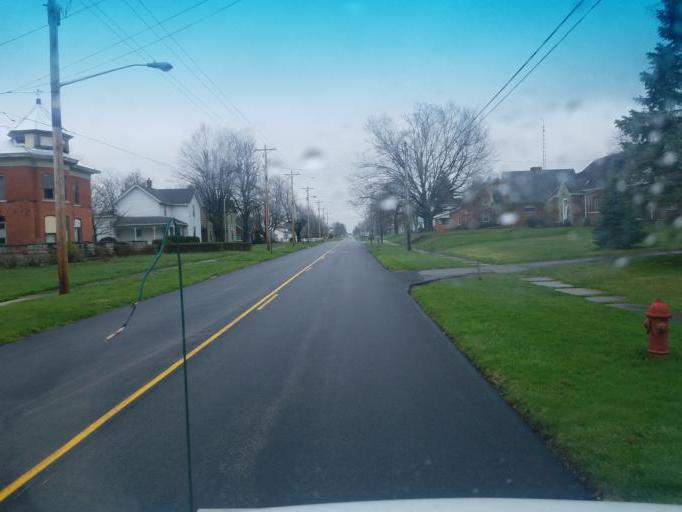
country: US
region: Ohio
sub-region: Huron County
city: Willard
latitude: 40.9605
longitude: -82.8486
